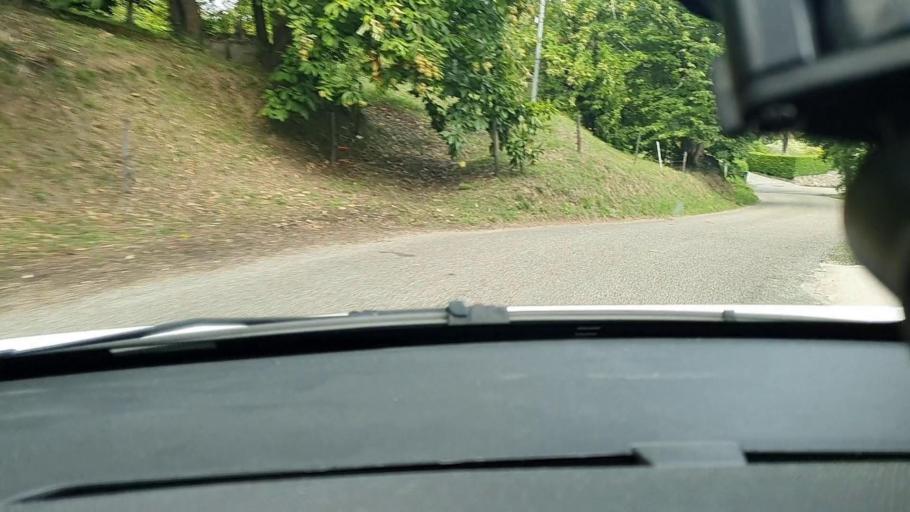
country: FR
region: Languedoc-Roussillon
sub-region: Departement du Gard
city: Branoux-les-Taillades
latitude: 44.2200
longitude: 3.9843
